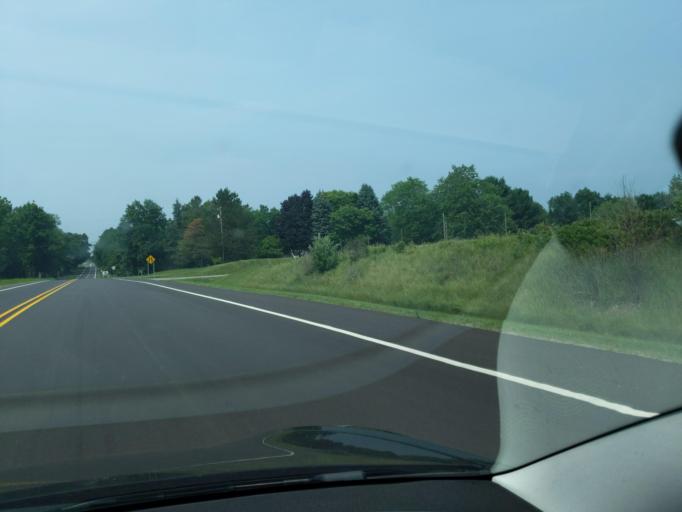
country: US
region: Michigan
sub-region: Clinton County
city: DeWitt
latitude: 42.8192
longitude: -84.5724
